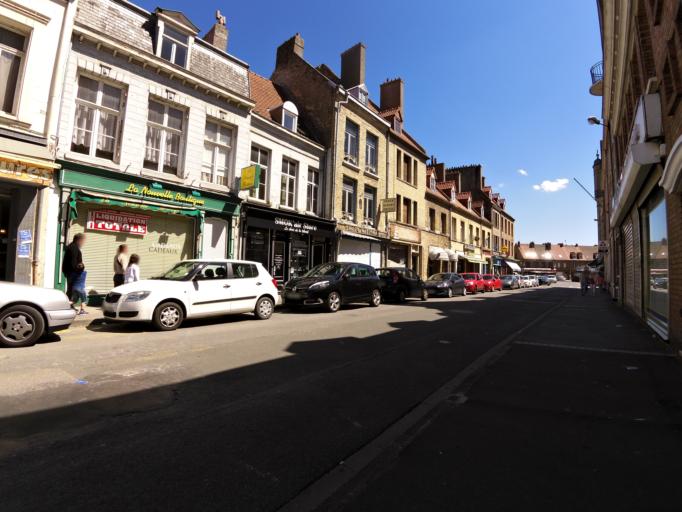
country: FR
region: Nord-Pas-de-Calais
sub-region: Departement du Nord
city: Bergues
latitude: 50.9692
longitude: 2.4324
